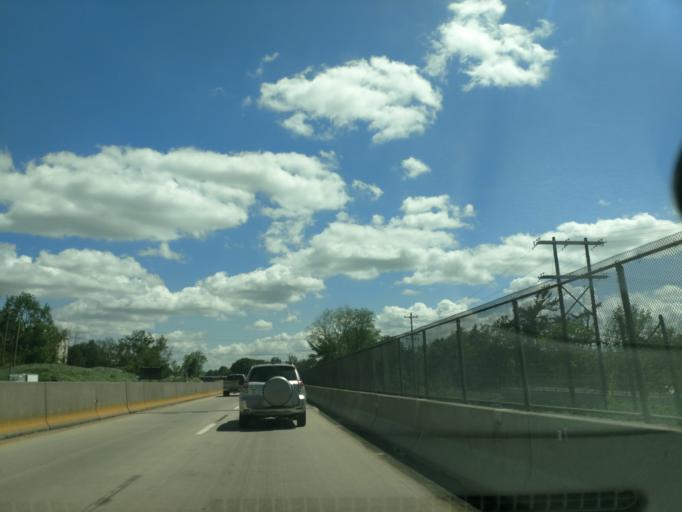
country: US
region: Pennsylvania
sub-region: Montgomery County
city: Audubon
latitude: 40.1072
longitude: -75.4201
